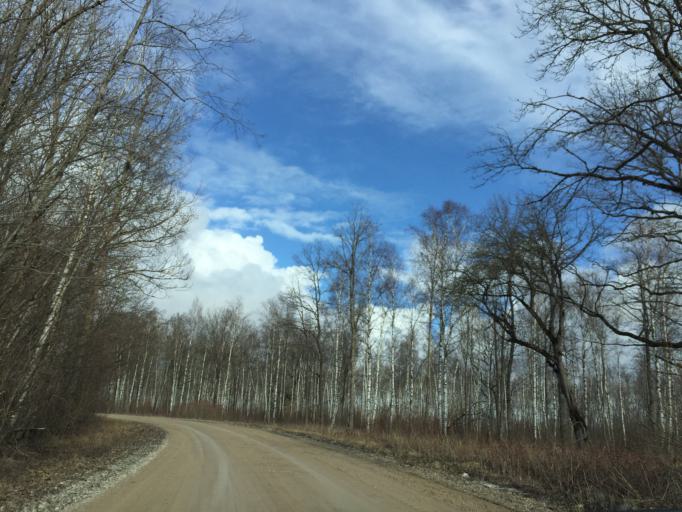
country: EE
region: Laeaene
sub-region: Lihula vald
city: Lihula
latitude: 58.7297
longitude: 23.8310
